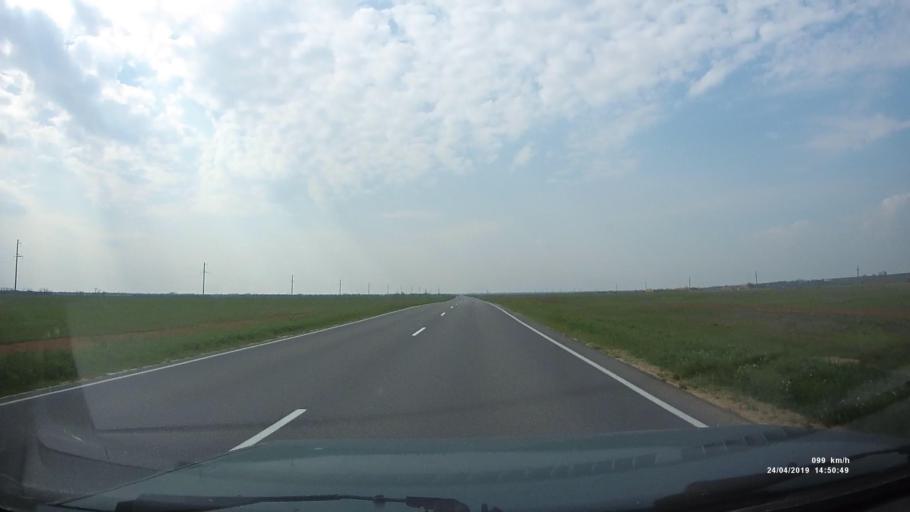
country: RU
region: Rostov
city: Remontnoye
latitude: 46.5203
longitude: 43.7124
